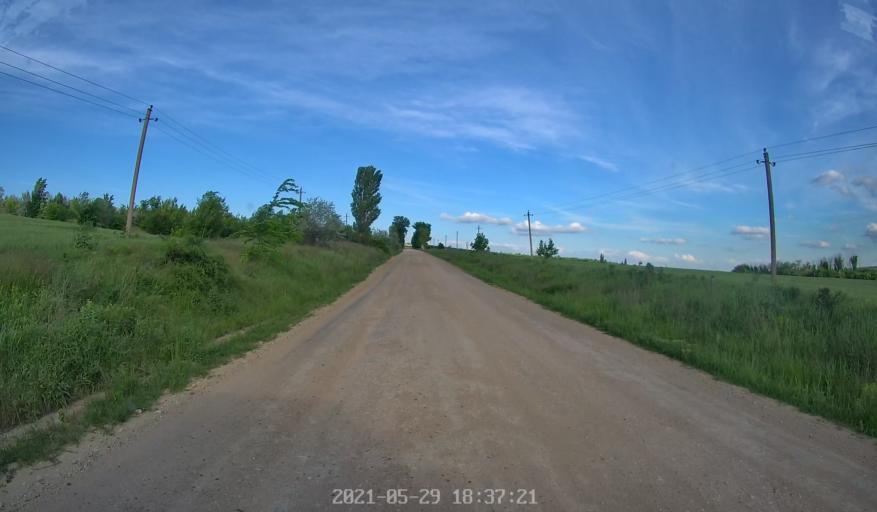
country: MD
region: Chisinau
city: Singera
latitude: 46.8044
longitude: 28.9303
